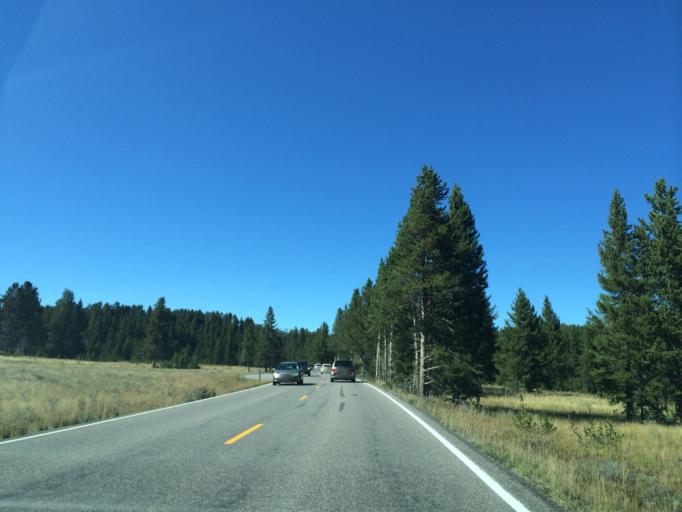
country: US
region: Montana
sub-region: Gallatin County
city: West Yellowstone
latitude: 44.6955
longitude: -110.5005
